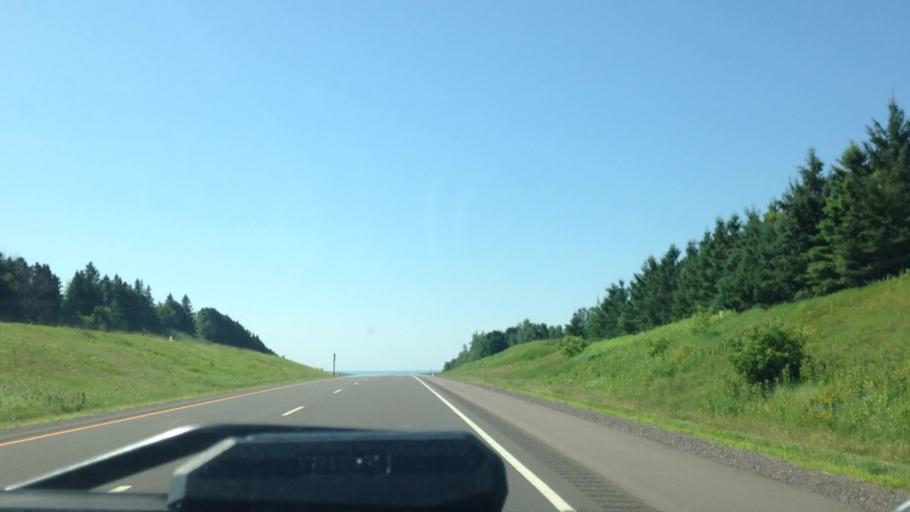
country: US
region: Wisconsin
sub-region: Washburn County
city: Spooner
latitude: 45.9605
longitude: -91.8282
